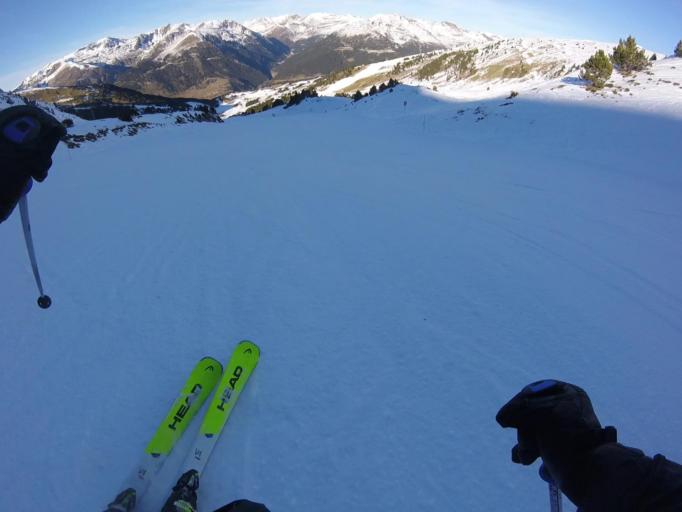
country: AD
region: Canillo
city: El Tarter
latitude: 42.5540
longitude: 1.6472
